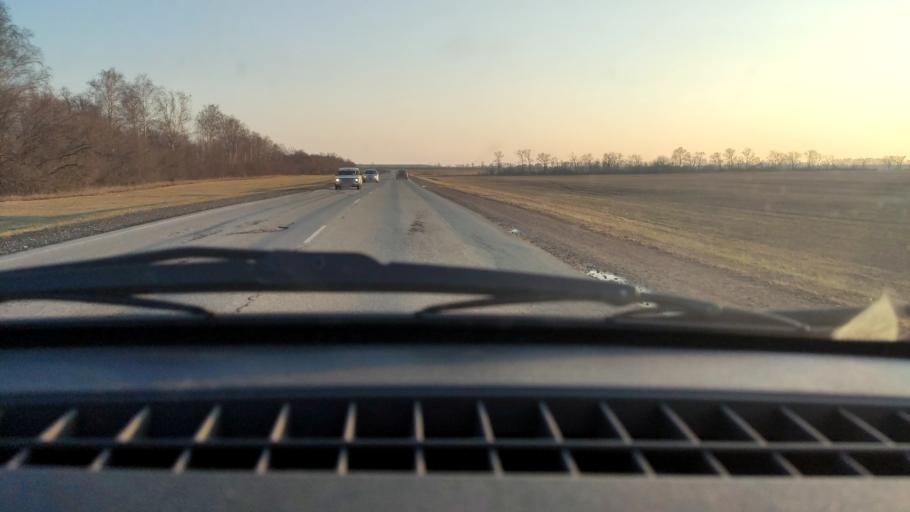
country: RU
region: Bashkortostan
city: Davlekanovo
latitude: 54.2835
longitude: 55.1122
